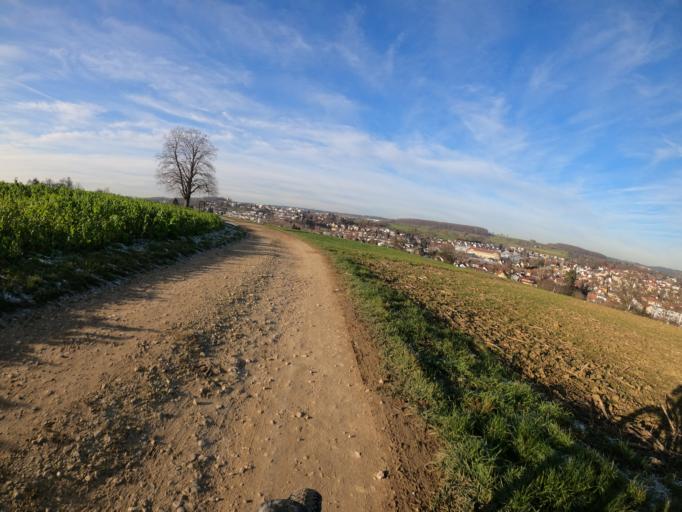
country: DE
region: Baden-Wuerttemberg
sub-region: Regierungsbezirk Stuttgart
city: Goeppingen
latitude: 48.7059
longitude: 9.6252
